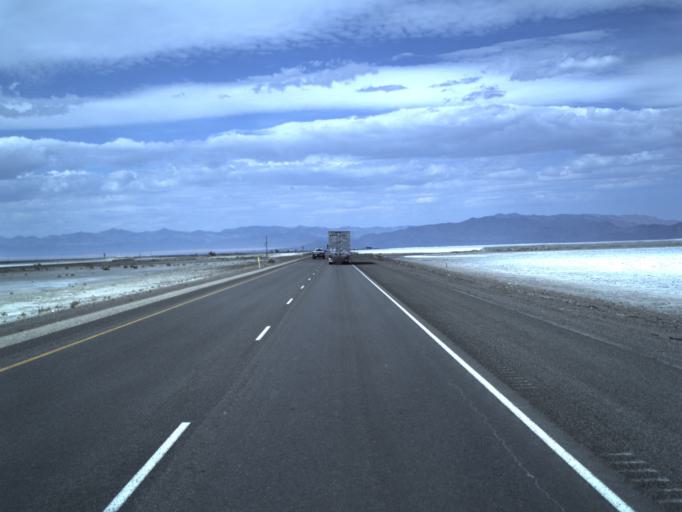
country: US
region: Utah
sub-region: Tooele County
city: Wendover
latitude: 40.7387
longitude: -113.8174
